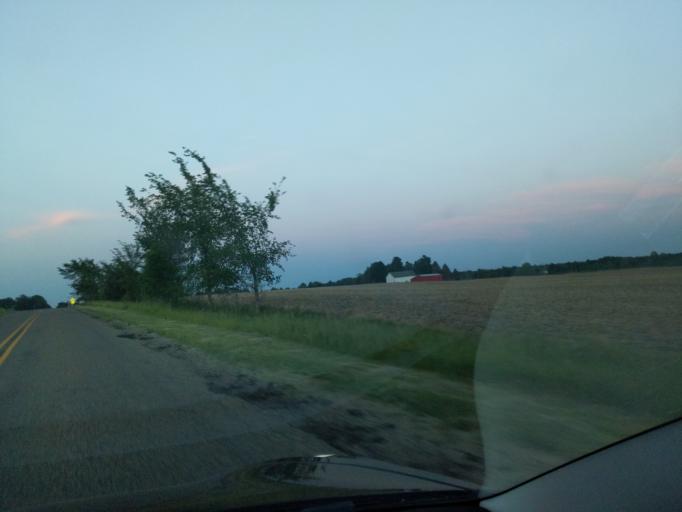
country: US
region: Michigan
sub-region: Eaton County
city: Olivet
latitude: 42.5389
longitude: -84.9593
